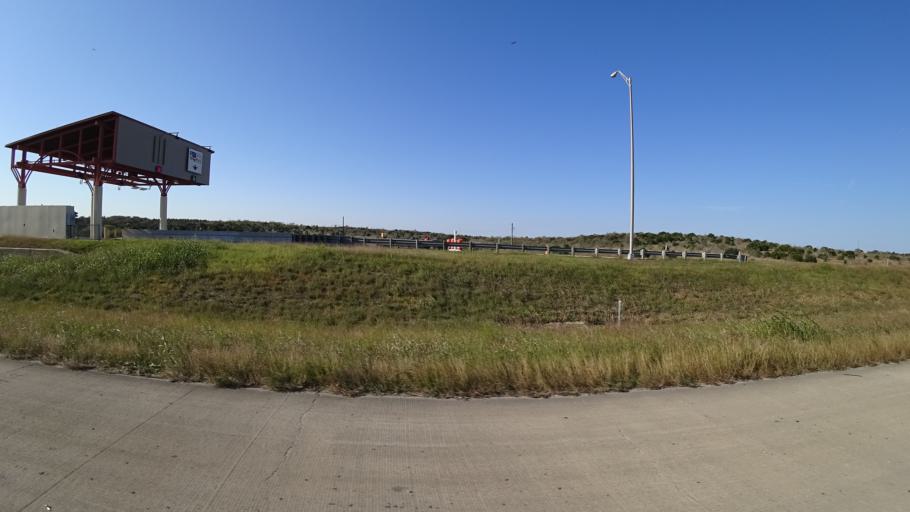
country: US
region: Texas
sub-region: Travis County
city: Manor
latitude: 30.3274
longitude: -97.5838
